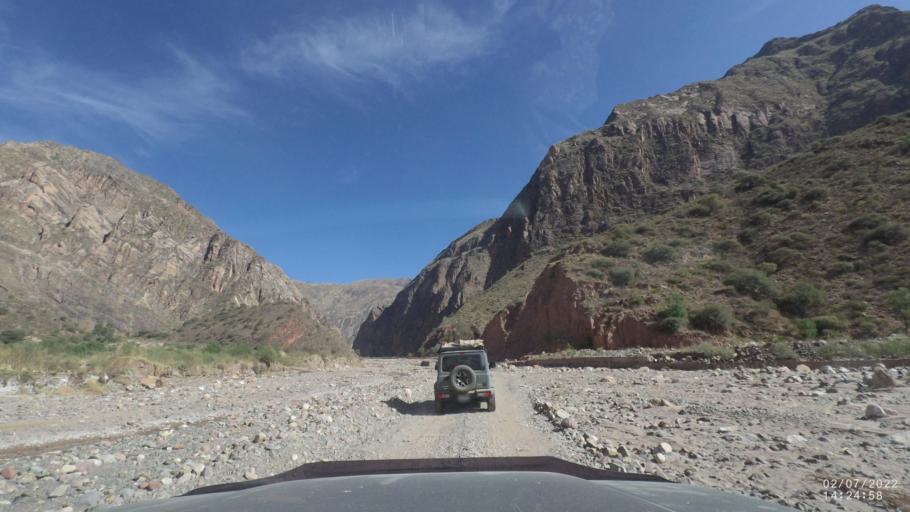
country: BO
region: Cochabamba
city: Irpa Irpa
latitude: -17.8340
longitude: -66.4142
